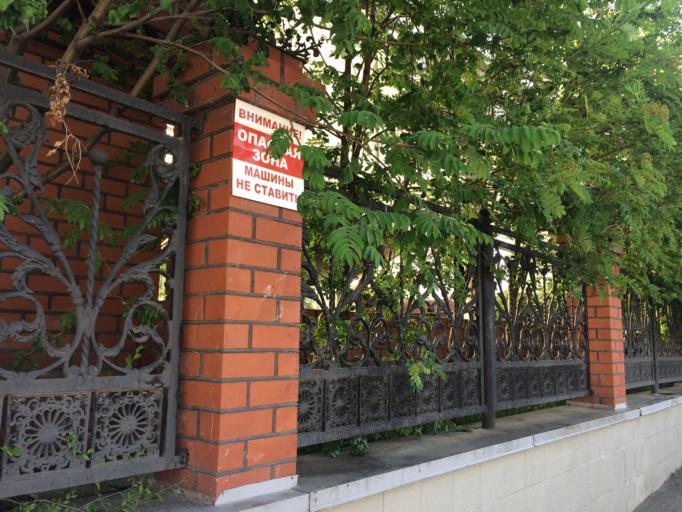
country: RU
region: Chelyabinsk
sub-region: Gorod Magnitogorsk
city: Magnitogorsk
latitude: 53.4000
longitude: 58.9863
